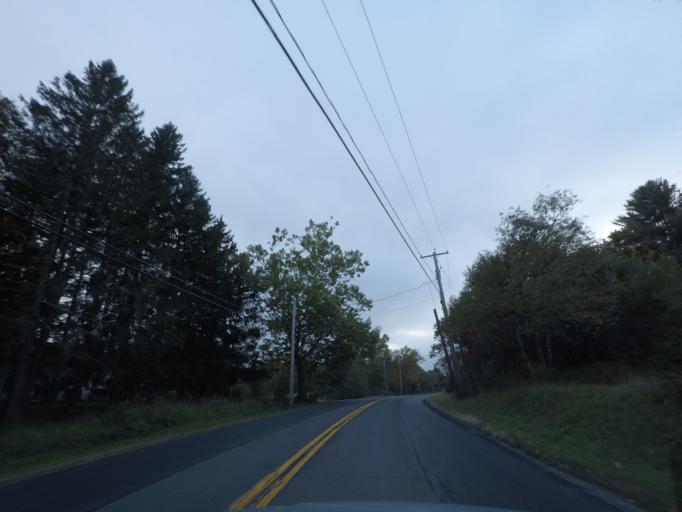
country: US
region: New York
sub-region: Rensselaer County
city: Nassau
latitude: 42.5601
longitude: -73.6453
